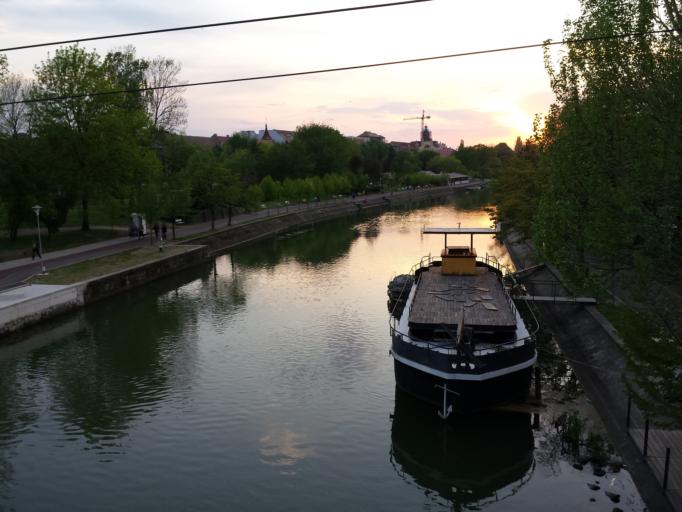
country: RO
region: Timis
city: Timisoara
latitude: 45.7489
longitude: 21.2255
